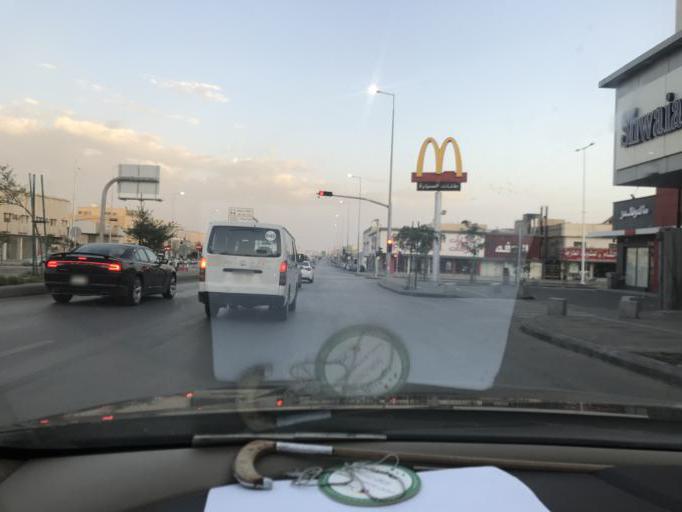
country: SA
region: Ar Riyad
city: Riyadh
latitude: 24.7535
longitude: 46.7695
